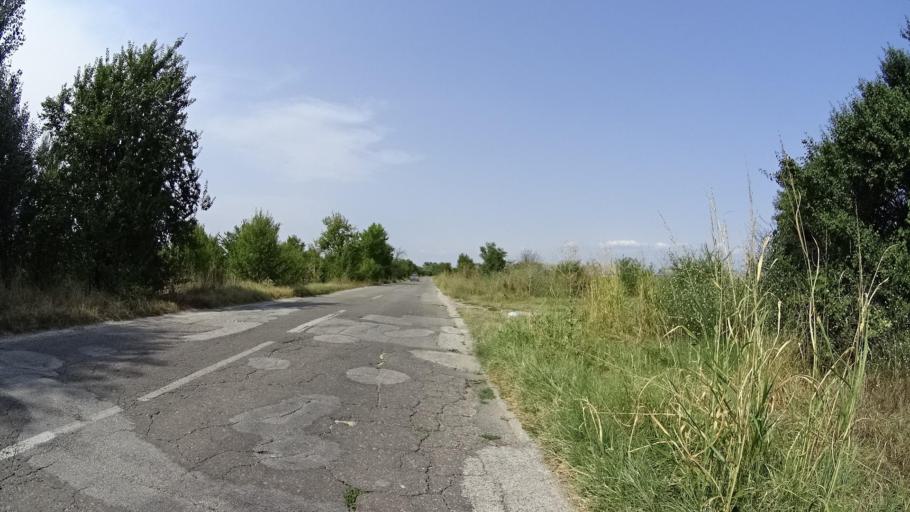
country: BG
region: Plovdiv
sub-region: Obshtina Plovdiv
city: Plovdiv
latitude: 42.2287
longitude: 24.7861
